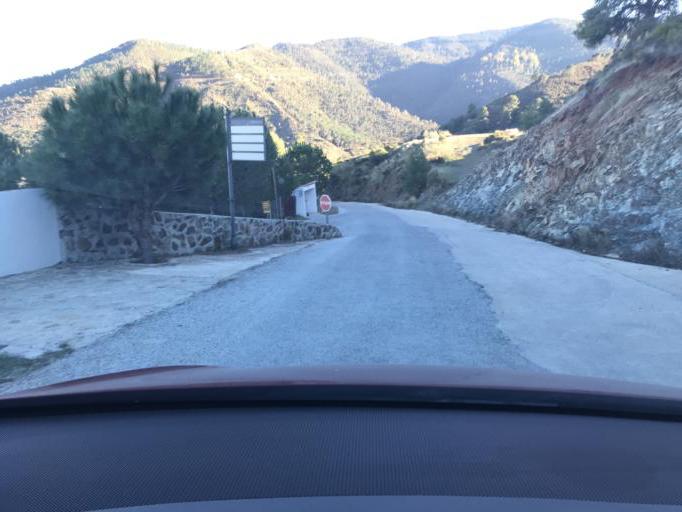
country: ES
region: Andalusia
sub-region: Provincia de Malaga
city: Tolox
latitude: 36.6845
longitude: -4.9110
